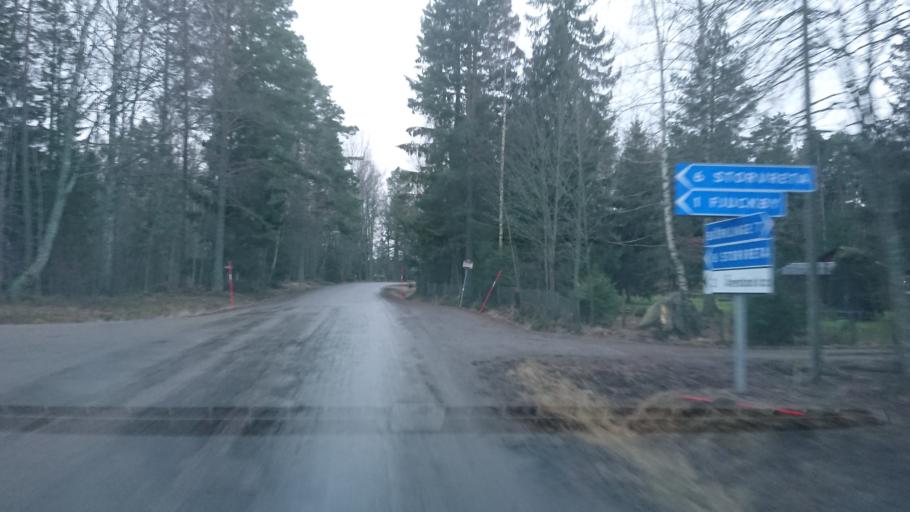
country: SE
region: Uppsala
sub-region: Osthammars Kommun
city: Bjorklinge
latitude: 59.9792
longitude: 17.5954
